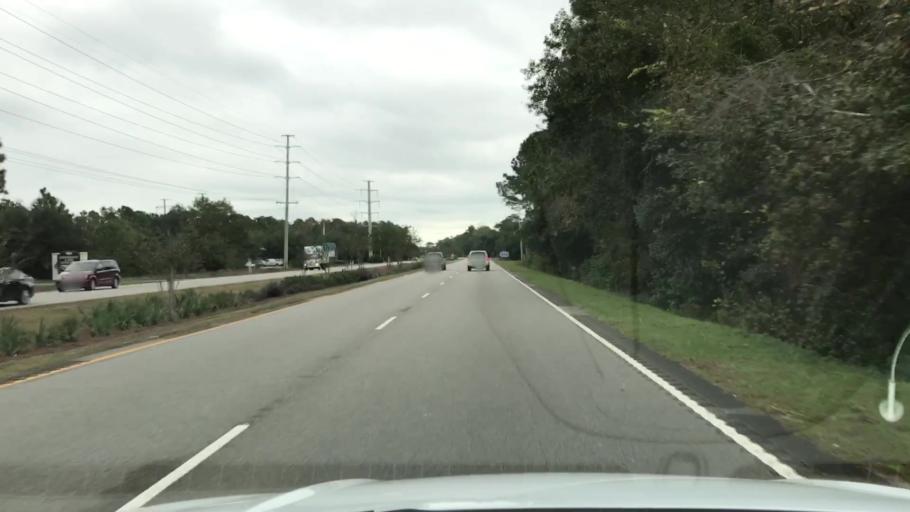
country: US
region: South Carolina
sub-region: Georgetown County
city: Georgetown
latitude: 33.4262
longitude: -79.1555
